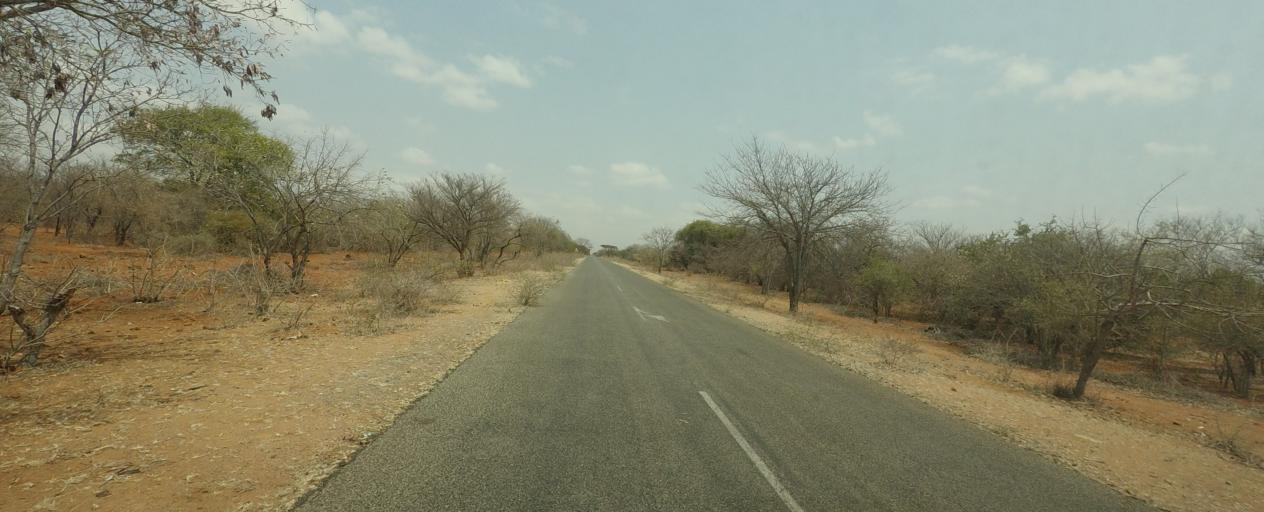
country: ZA
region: Limpopo
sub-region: Vhembe District Municipality
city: Mutale
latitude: -22.4210
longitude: 30.9237
